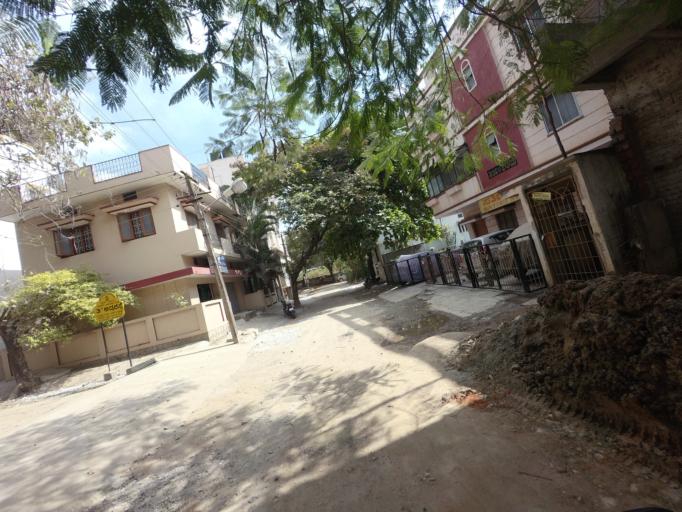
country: IN
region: Karnataka
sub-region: Bangalore Urban
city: Bangalore
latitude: 12.9601
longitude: 77.5358
